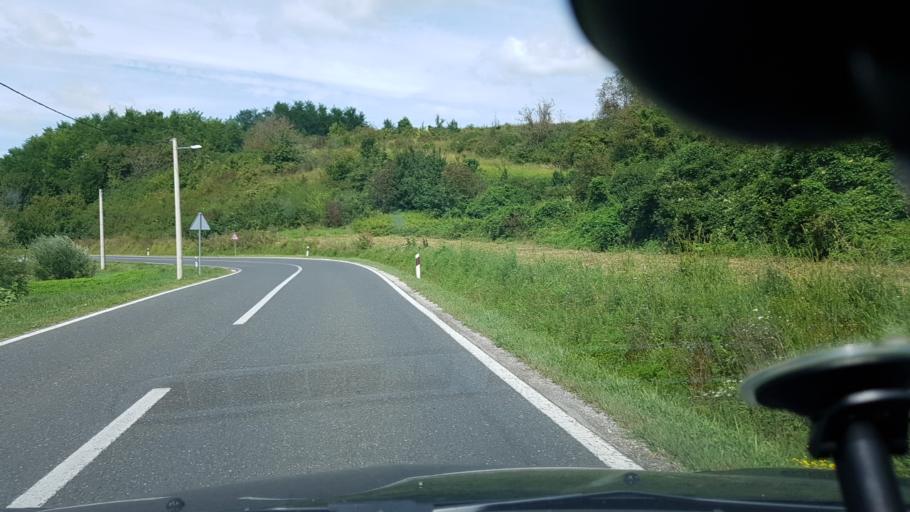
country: HR
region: Varazdinska
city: Lepoglava
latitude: 46.2098
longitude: 16.0208
